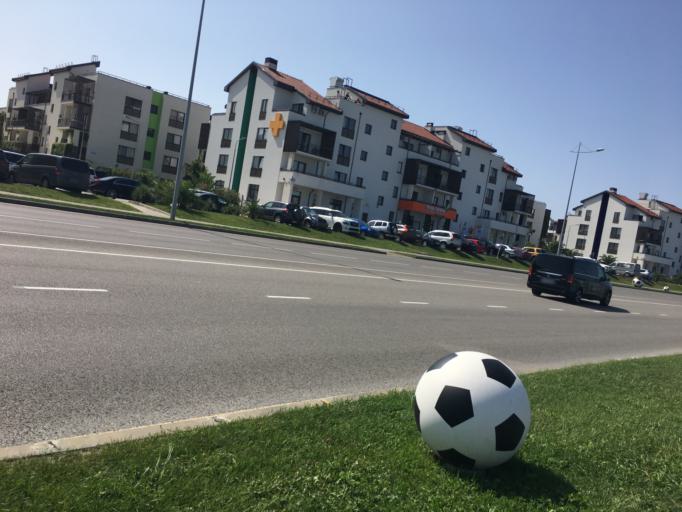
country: RU
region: Krasnodarskiy
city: Adler
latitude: 43.4118
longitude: 39.9432
